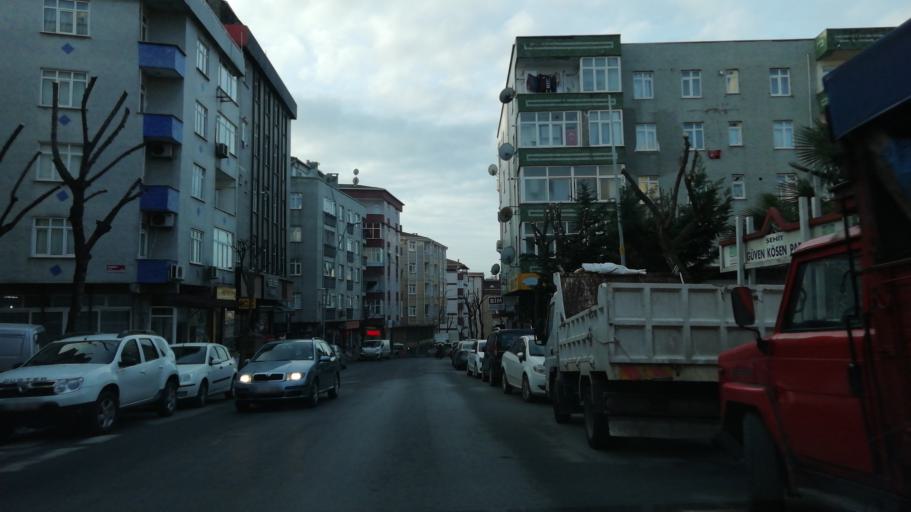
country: TR
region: Istanbul
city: Bahcelievler
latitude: 41.0066
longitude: 28.8277
